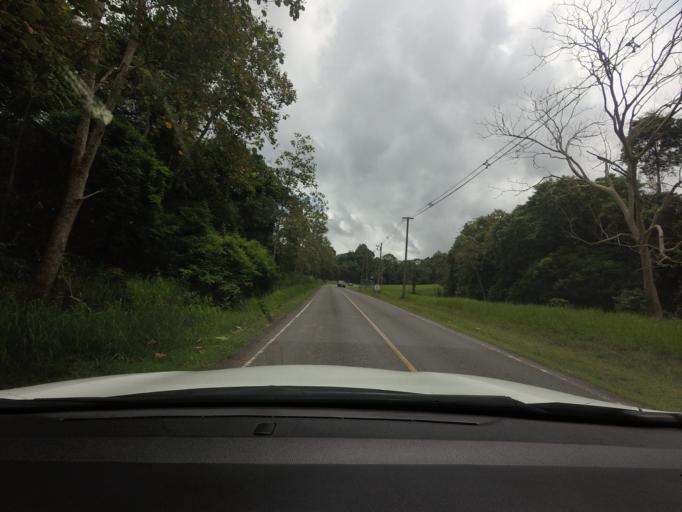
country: TH
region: Nakhon Ratchasima
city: Pak Chong
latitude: 14.4534
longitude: 101.3716
